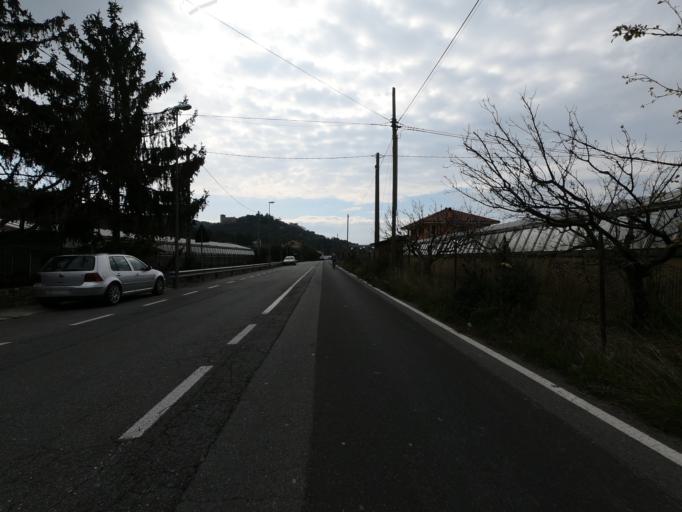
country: IT
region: Liguria
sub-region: Provincia di Savona
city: Andora
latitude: 43.9711
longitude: 8.1392
